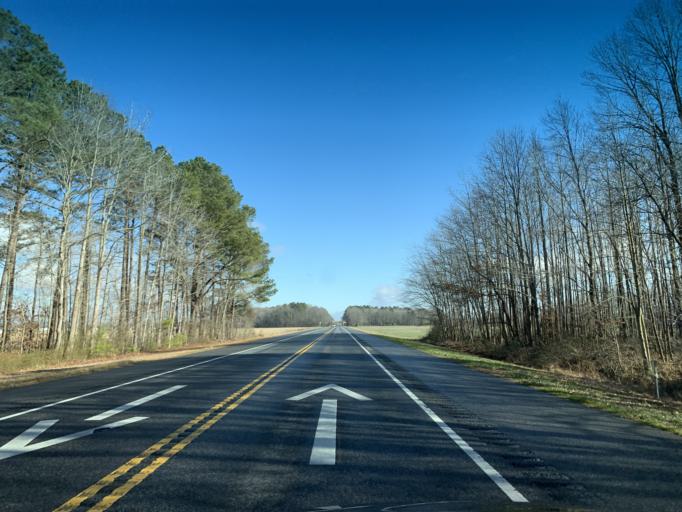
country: US
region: Maryland
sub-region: Worcester County
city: Berlin
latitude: 38.3706
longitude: -75.2634
